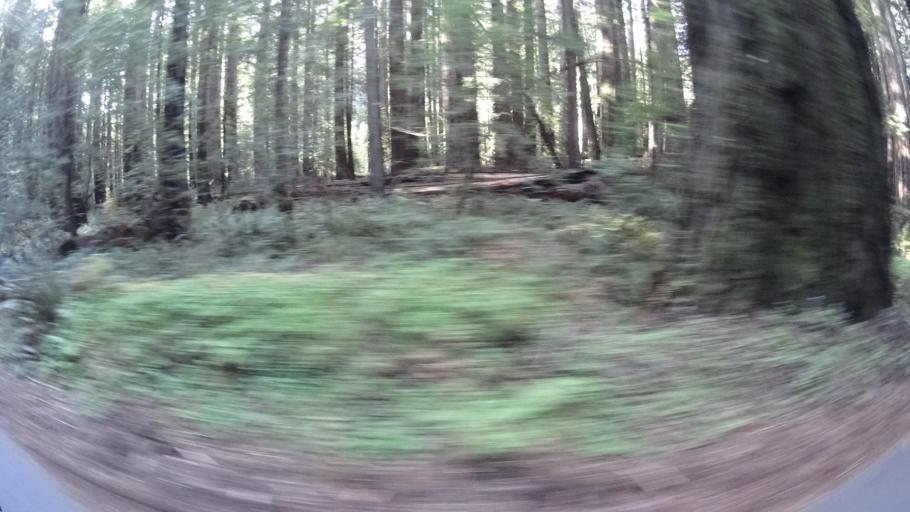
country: US
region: California
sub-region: Humboldt County
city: Rio Dell
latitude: 40.3516
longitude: -123.9964
